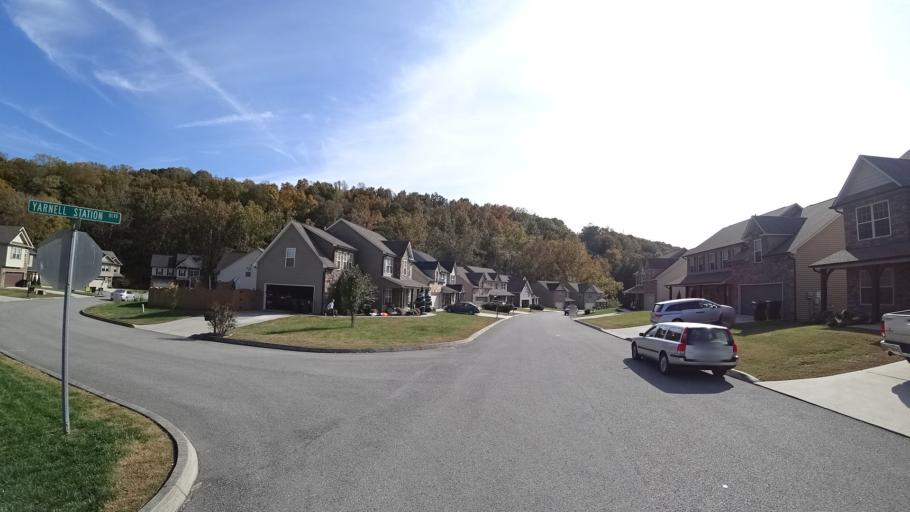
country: US
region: Tennessee
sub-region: Knox County
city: Farragut
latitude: 35.9270
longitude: -84.1595
